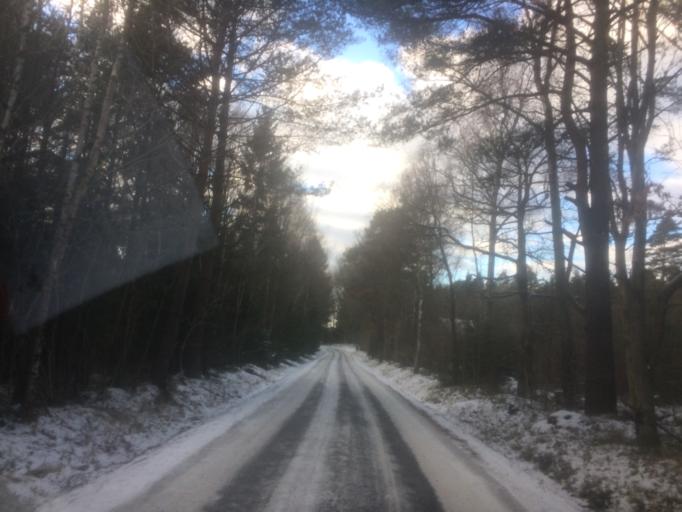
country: SE
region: Vaestra Goetaland
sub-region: Ale Kommun
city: Surte
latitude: 57.8269
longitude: 11.9821
